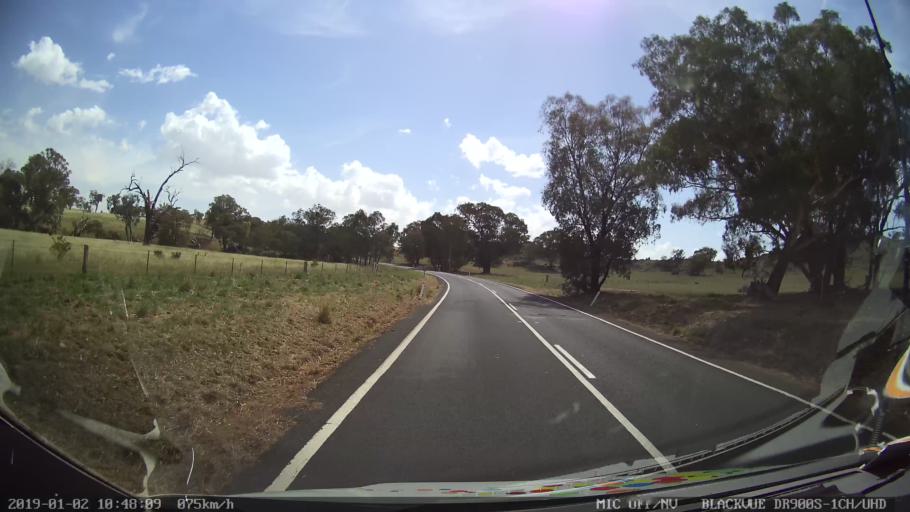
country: AU
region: New South Wales
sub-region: Cootamundra
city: Cootamundra
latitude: -34.7391
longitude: 148.2759
